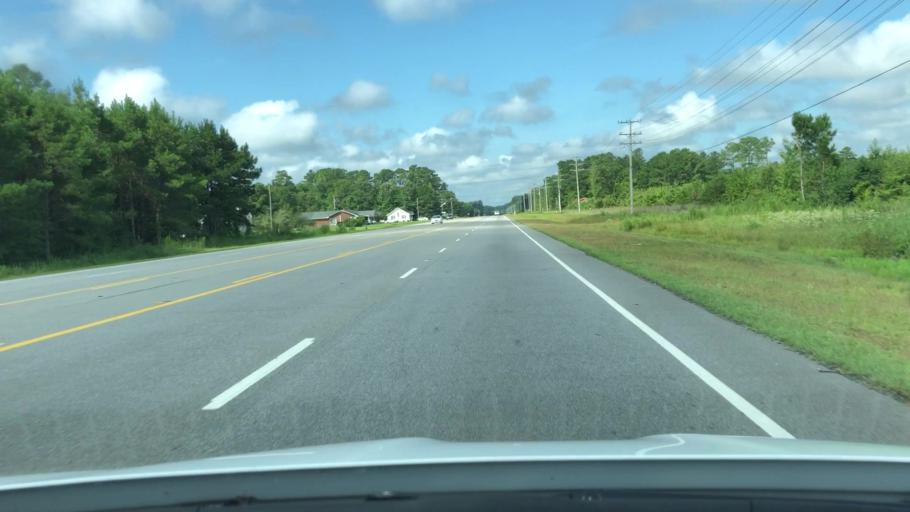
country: US
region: North Carolina
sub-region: Bertie County
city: Windsor
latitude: 36.0248
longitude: -76.8130
